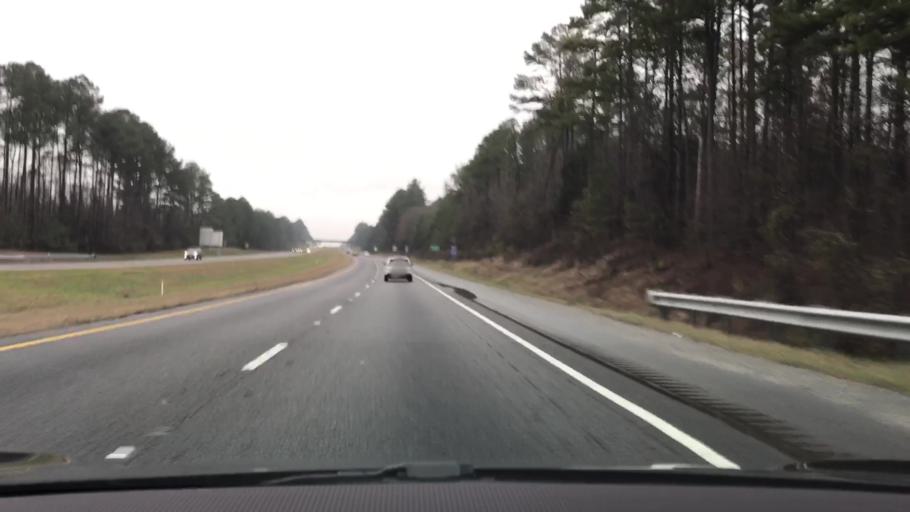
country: US
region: Georgia
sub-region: Walton County
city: Social Circle
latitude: 33.6111
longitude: -83.7093
